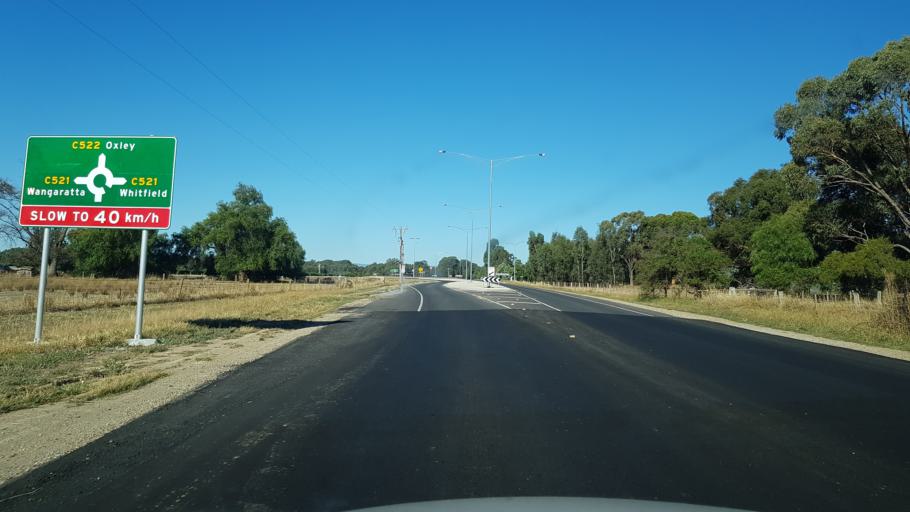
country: AU
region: Victoria
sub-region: Wangaratta
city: Wangaratta
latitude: -36.4397
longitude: 146.3582
